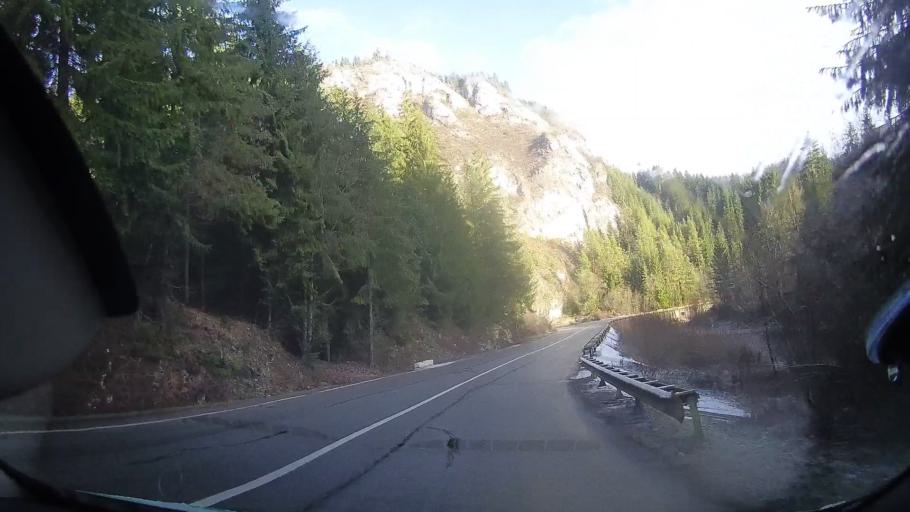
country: RO
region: Alba
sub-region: Comuna Albac
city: Albac
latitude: 46.4558
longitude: 22.9213
